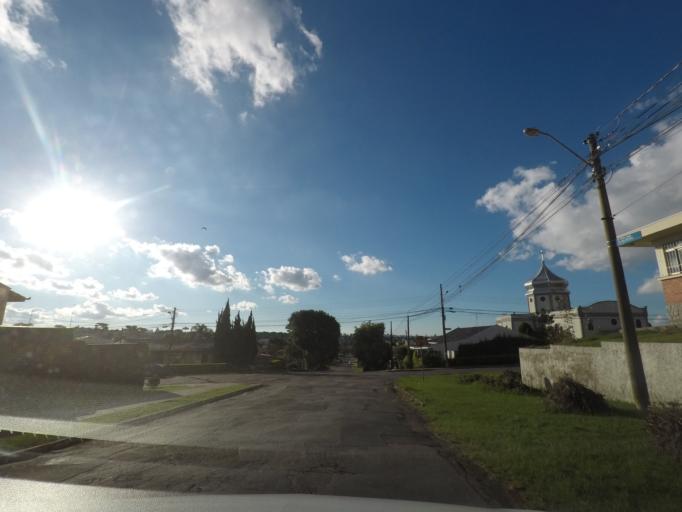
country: BR
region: Parana
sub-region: Sao Jose Dos Pinhais
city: Sao Jose dos Pinhais
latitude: -25.4988
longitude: -49.2528
